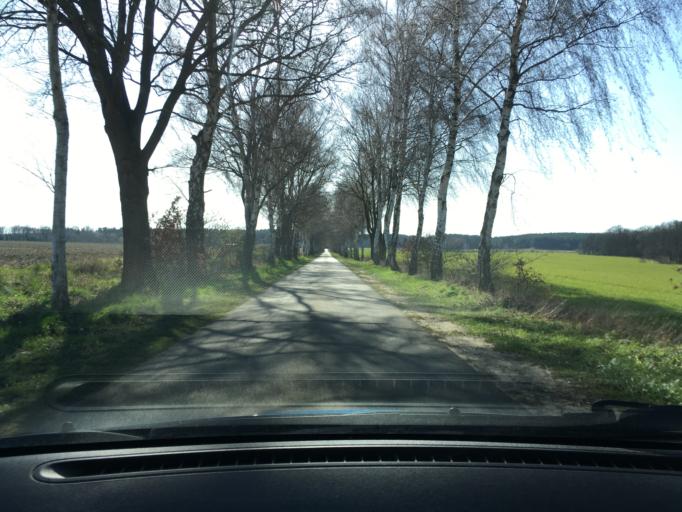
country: DE
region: Lower Saxony
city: Barnstedt
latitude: 53.1516
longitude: 10.3723
